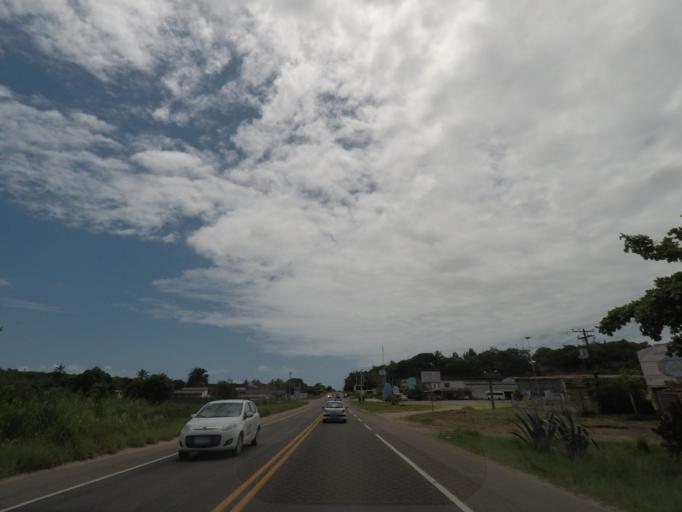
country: BR
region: Bahia
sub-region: Itaparica
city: Itaparica
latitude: -12.9532
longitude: -38.6323
